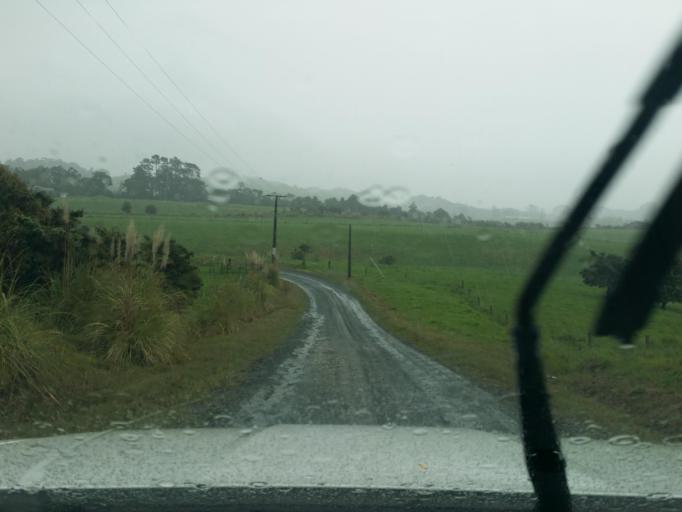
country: NZ
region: Northland
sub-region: Kaipara District
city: Dargaville
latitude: -35.8845
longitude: 173.9941
